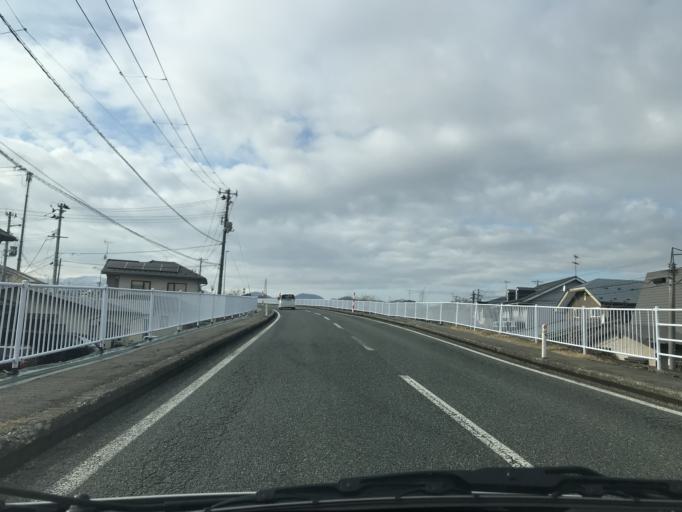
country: JP
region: Iwate
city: Hanamaki
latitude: 39.4058
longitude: 141.1138
